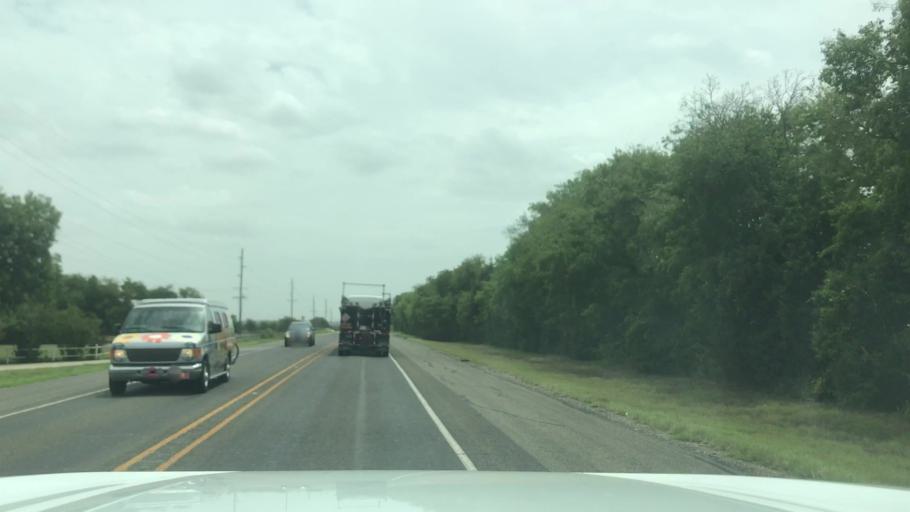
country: US
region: Texas
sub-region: Bosque County
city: Valley Mills
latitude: 31.6890
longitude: -97.5318
